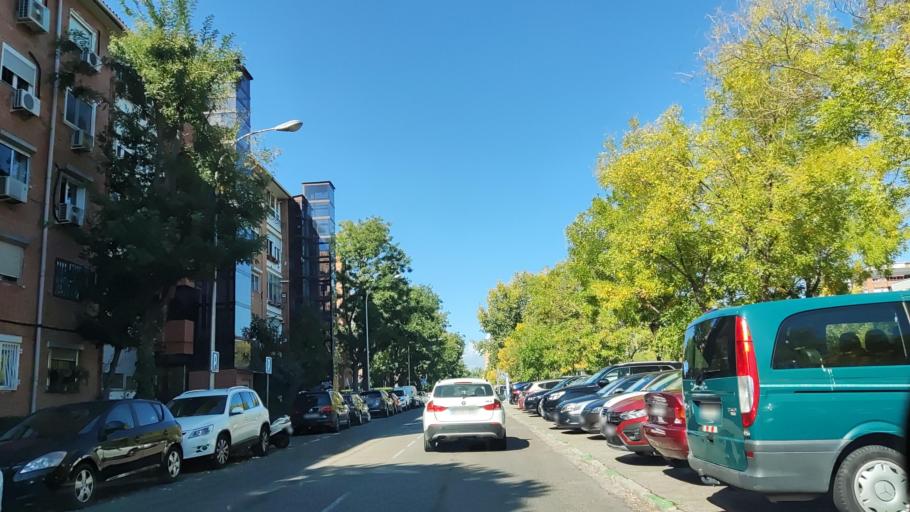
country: ES
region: Madrid
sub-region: Provincia de Madrid
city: Moncloa-Aravaca
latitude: 40.4270
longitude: -3.7302
